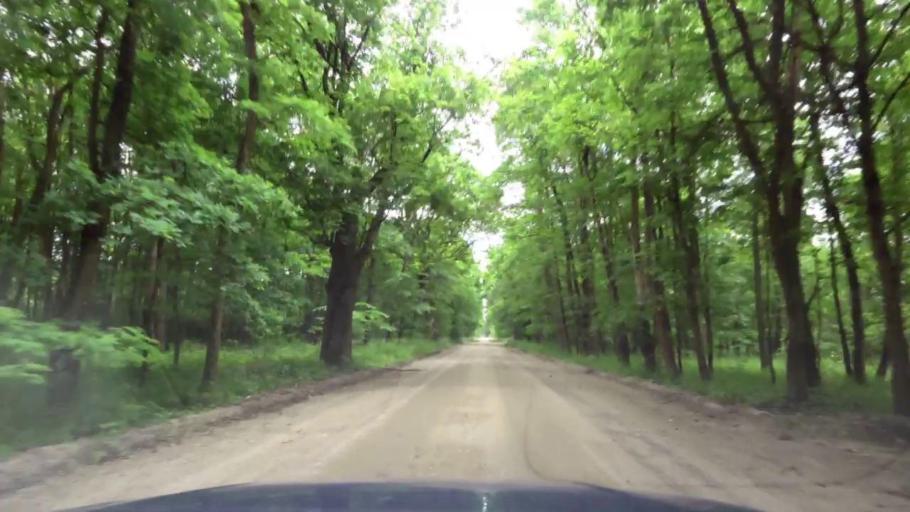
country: PL
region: West Pomeranian Voivodeship
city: Trzcinsko Zdroj
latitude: 52.8707
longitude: 14.5845
